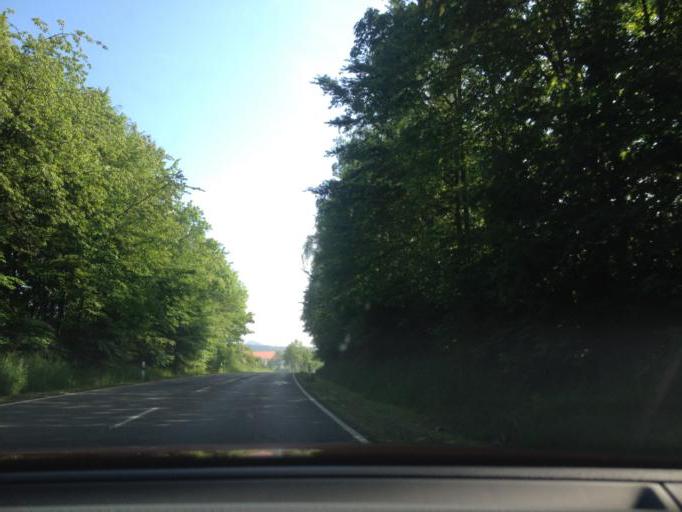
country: DE
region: Bavaria
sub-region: Upper Palatinate
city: Speinshart
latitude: 49.7798
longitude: 11.8157
